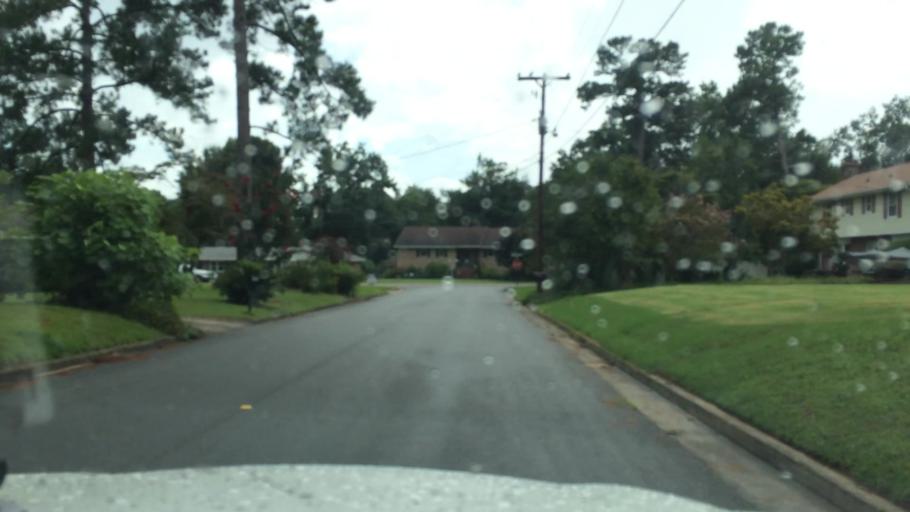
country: US
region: South Carolina
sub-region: Aiken County
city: North Augusta
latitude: 33.5058
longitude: -81.9871
